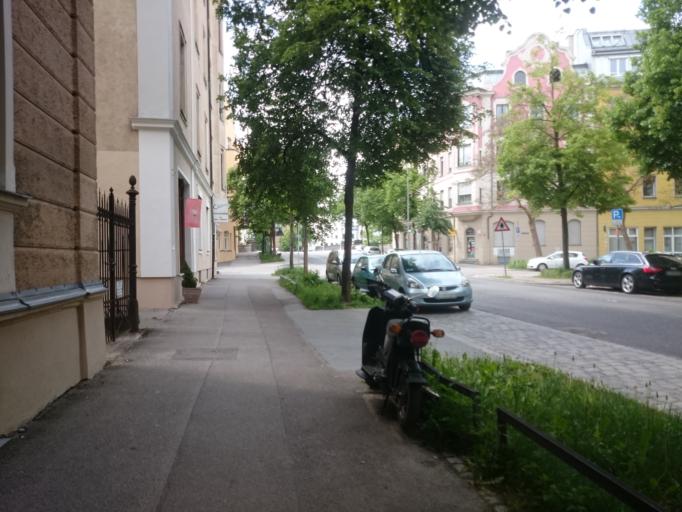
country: DE
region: Bavaria
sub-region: Swabia
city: Augsburg
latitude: 48.3577
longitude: 10.8973
